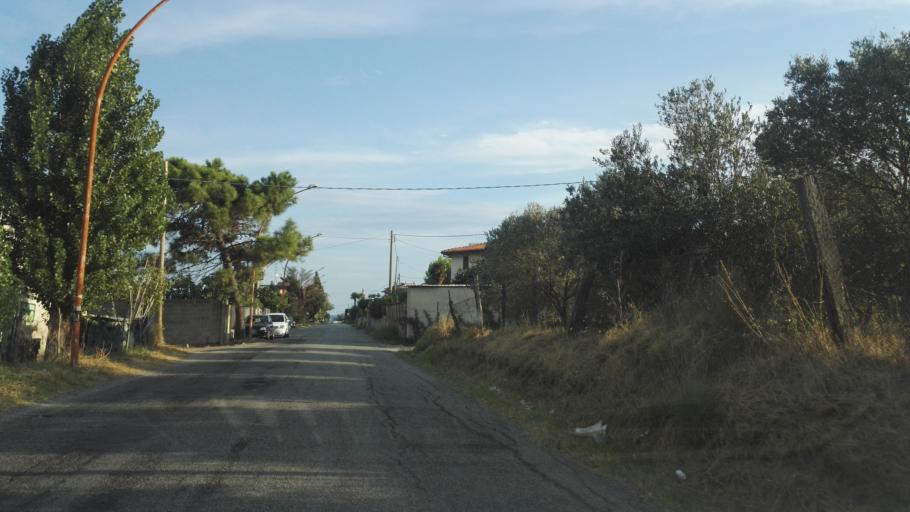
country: IT
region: Calabria
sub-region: Provincia di Reggio Calabria
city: Caulonia Marina
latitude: 38.3619
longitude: 16.4853
